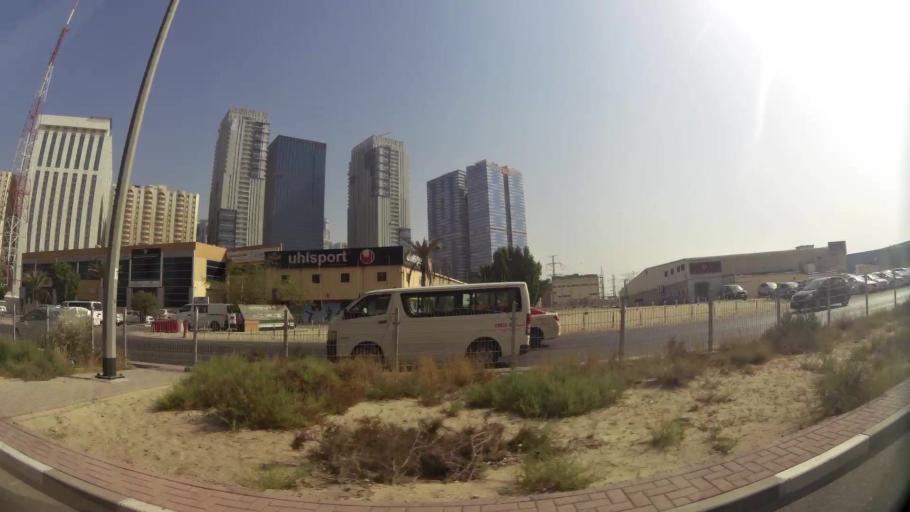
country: AE
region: Ash Shariqah
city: Sharjah
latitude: 25.2981
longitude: 55.3834
